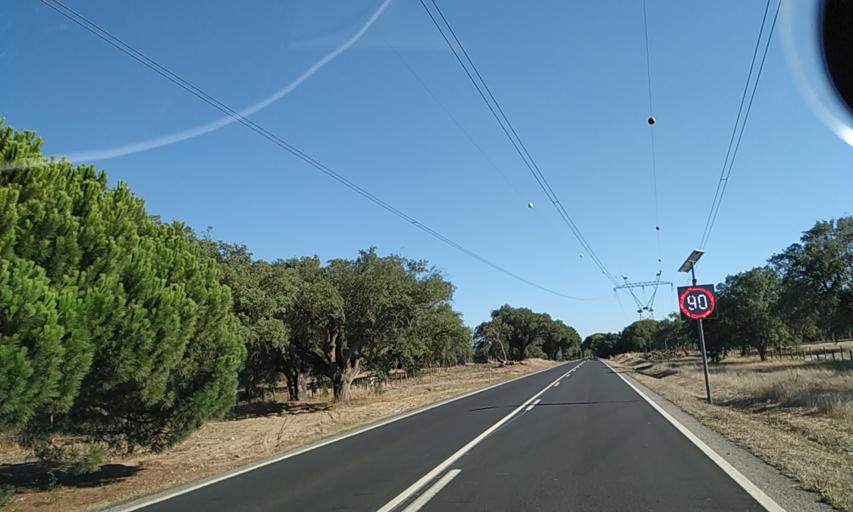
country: PT
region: Santarem
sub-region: Benavente
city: Poceirao
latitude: 38.8475
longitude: -8.8811
